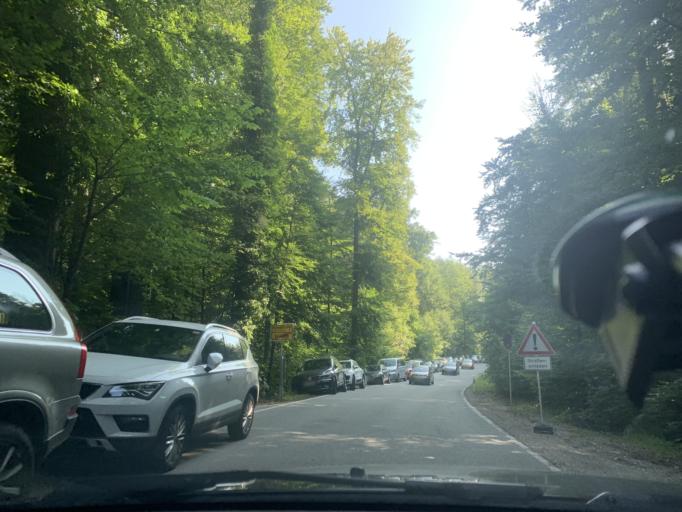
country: DE
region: Bavaria
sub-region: Upper Bavaria
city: Feldafing
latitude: 47.9530
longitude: 11.3029
